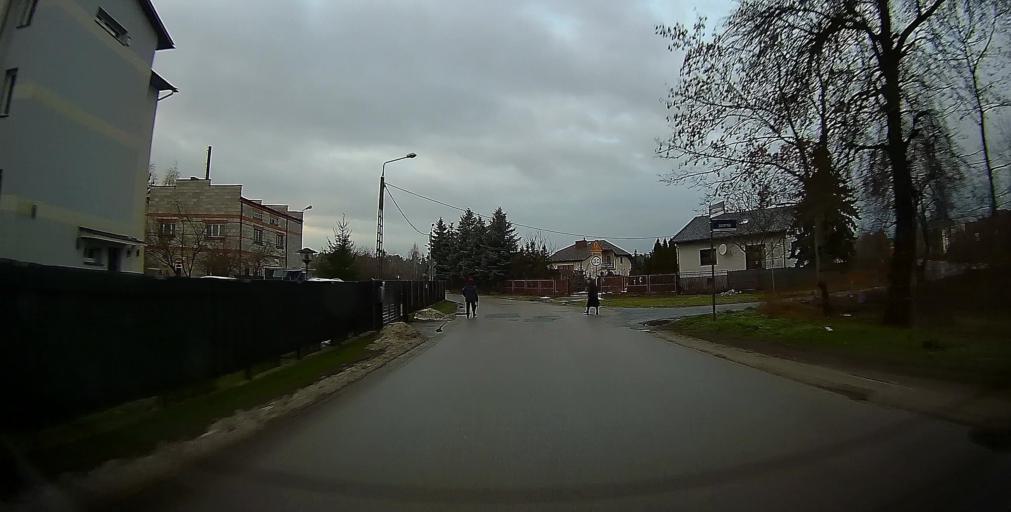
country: PL
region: Masovian Voivodeship
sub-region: Radom
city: Radom
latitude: 51.4489
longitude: 21.1383
